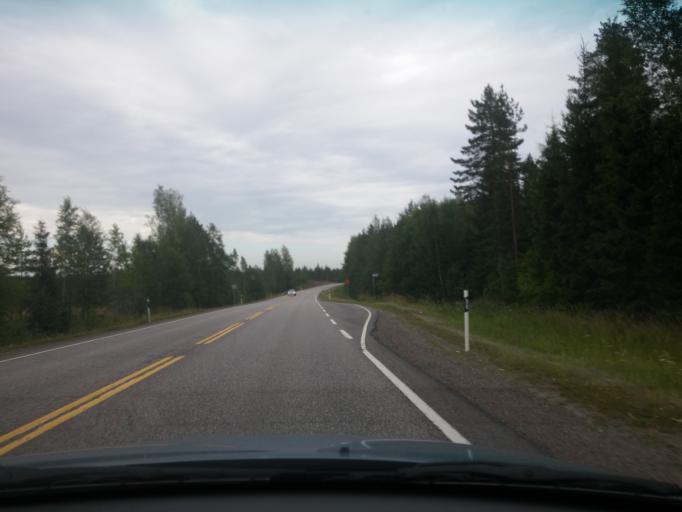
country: FI
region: Haeme
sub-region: Riihimaeki
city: Loppi
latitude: 60.7379
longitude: 24.3715
